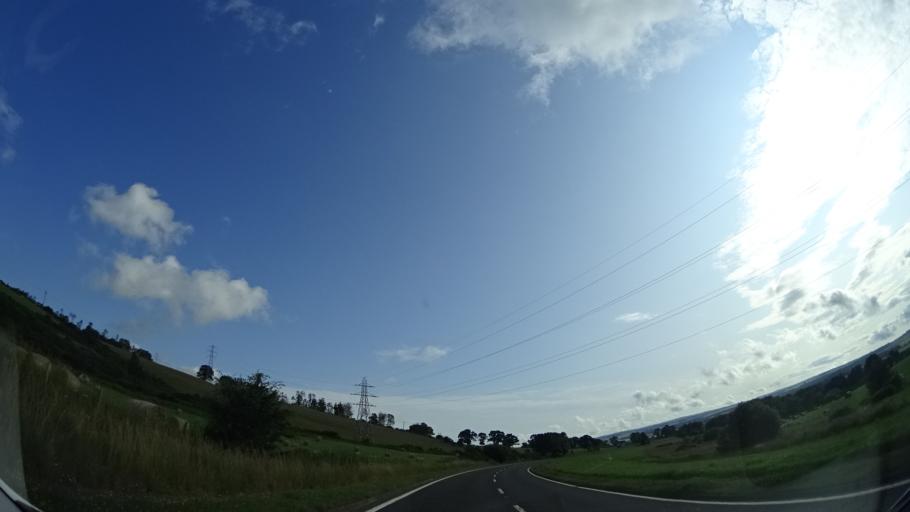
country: GB
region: Scotland
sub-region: Highland
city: Conon Bridge
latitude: 57.5785
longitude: -4.4454
